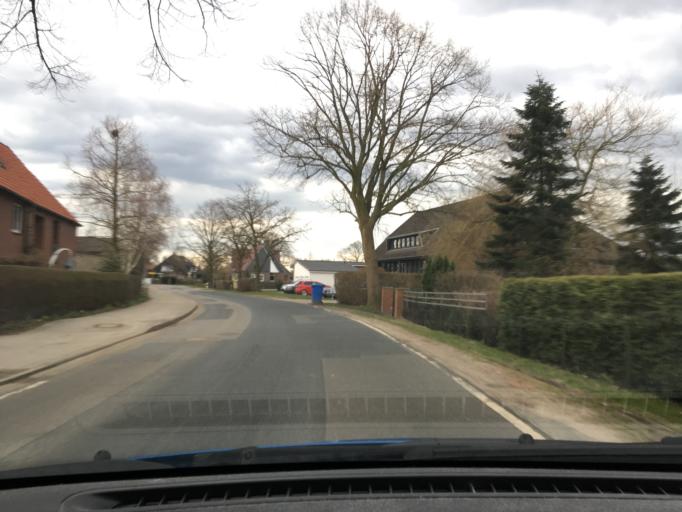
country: DE
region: Lower Saxony
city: Drage
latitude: 53.3743
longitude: 10.2574
